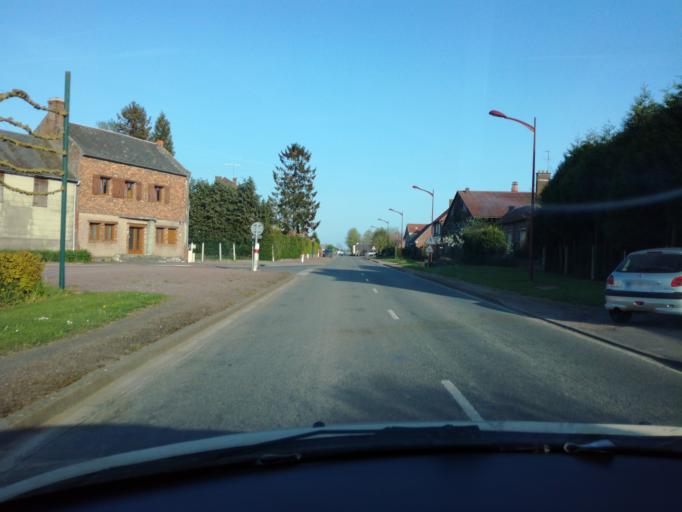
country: FR
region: Picardie
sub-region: Departement de la Somme
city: Hornoy-le-Bourg
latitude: 49.8260
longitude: 1.9417
